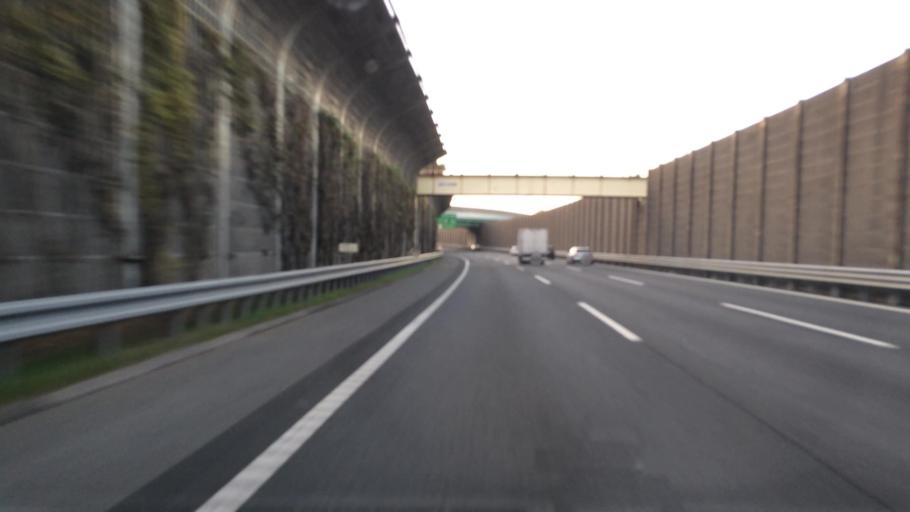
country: JP
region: Chiba
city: Chiba
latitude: 35.6471
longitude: 140.0650
